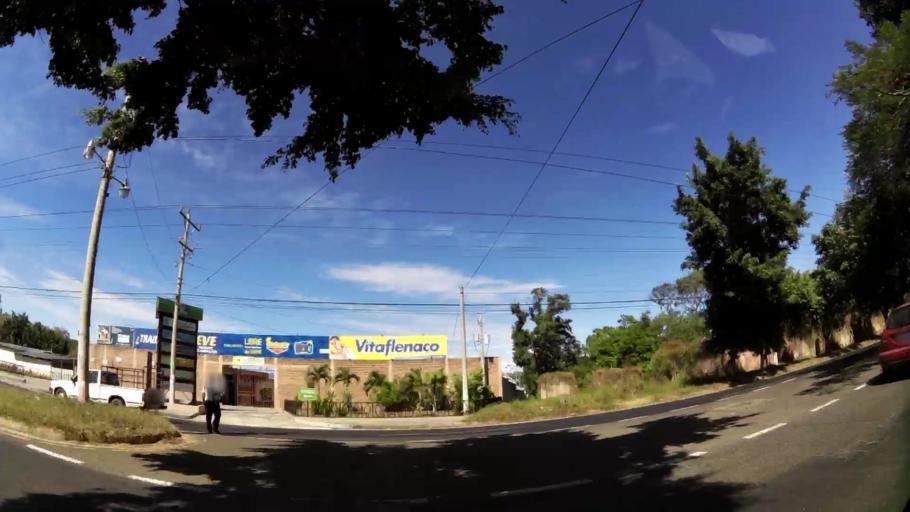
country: SV
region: Santa Ana
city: Chalchuapa
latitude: 13.9885
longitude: -89.6766
